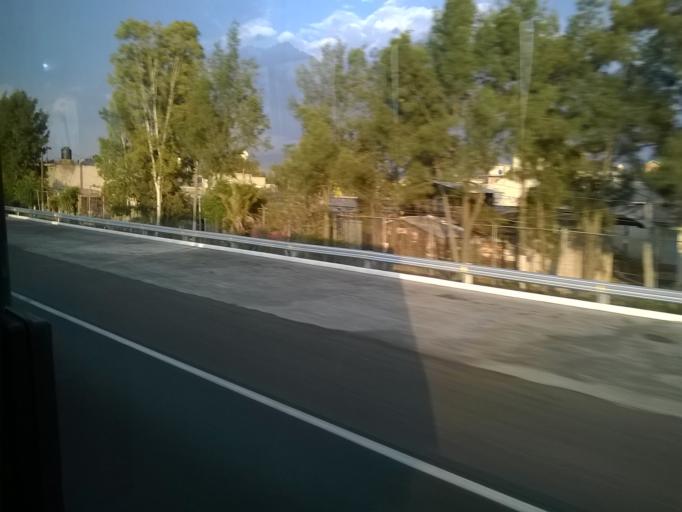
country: MX
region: Mexico
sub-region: Tecamac
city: Tecamac de Felipe Villanueva
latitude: 19.7147
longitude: -98.9622
